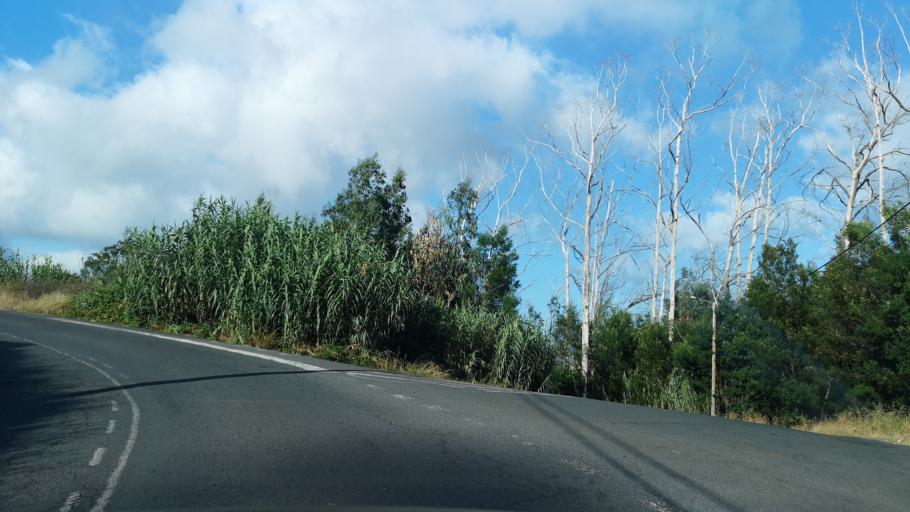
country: PT
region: Madeira
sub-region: Santa Cruz
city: Camacha
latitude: 32.6664
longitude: -16.8365
